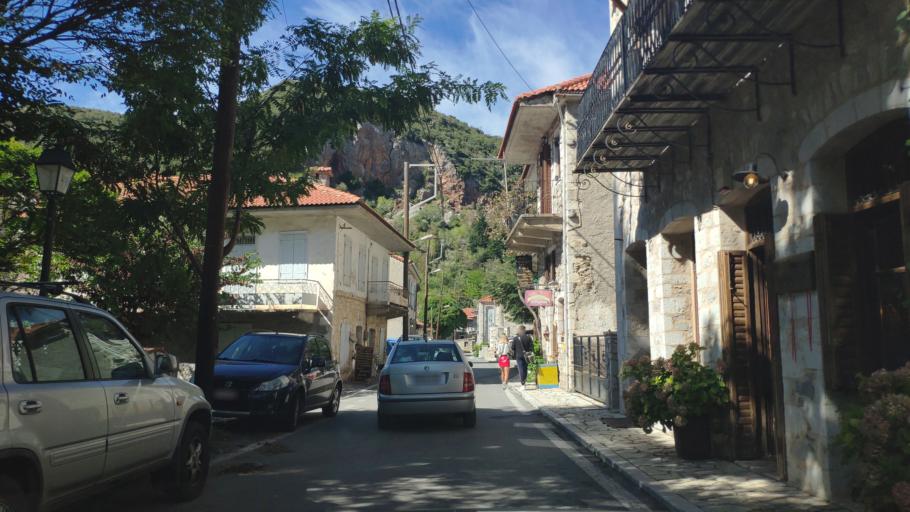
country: GR
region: Peloponnese
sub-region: Nomos Arkadias
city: Dimitsana
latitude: 37.5550
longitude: 22.0825
